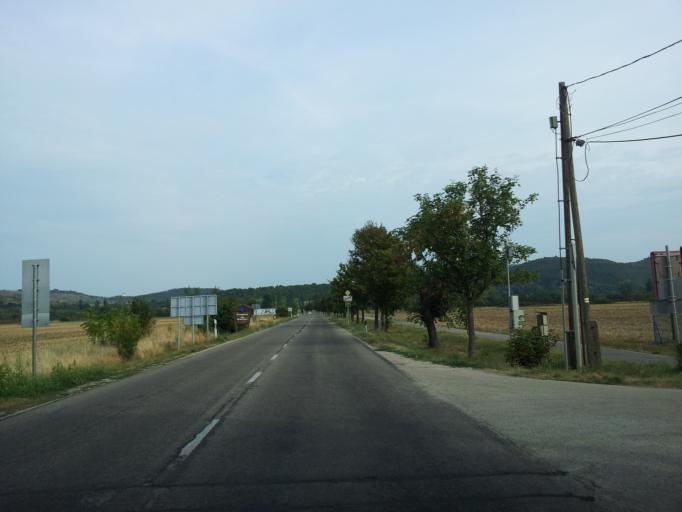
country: HU
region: Veszprem
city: Balatonfured
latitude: 46.9250
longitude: 17.8401
